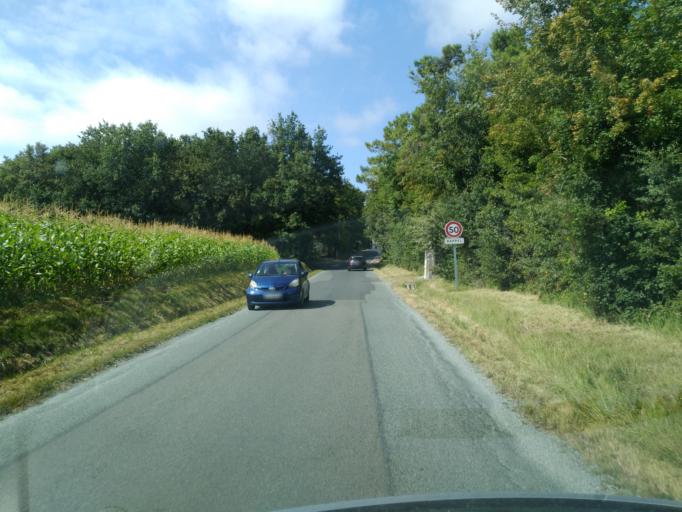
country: FR
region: Poitou-Charentes
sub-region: Departement de la Charente-Maritime
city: Breuillet
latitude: 45.6991
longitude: -1.0600
